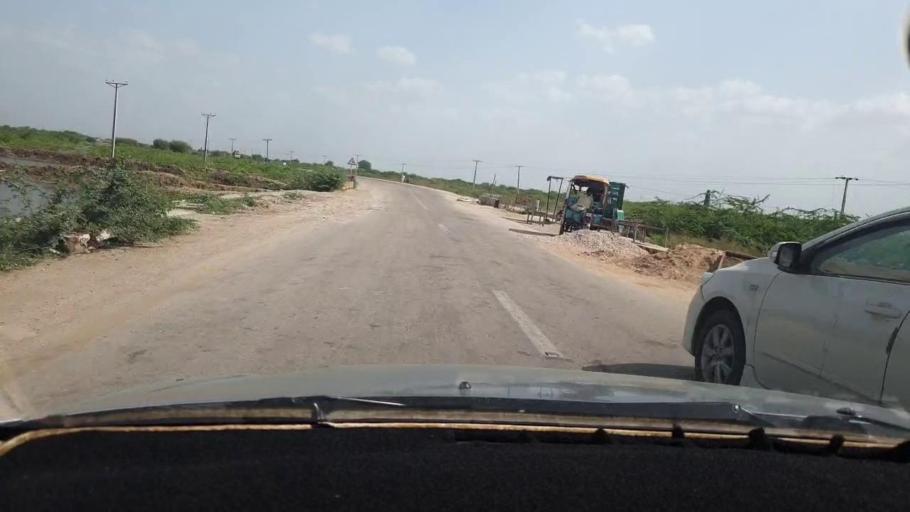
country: PK
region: Sindh
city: Naukot
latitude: 24.9007
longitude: 69.3317
